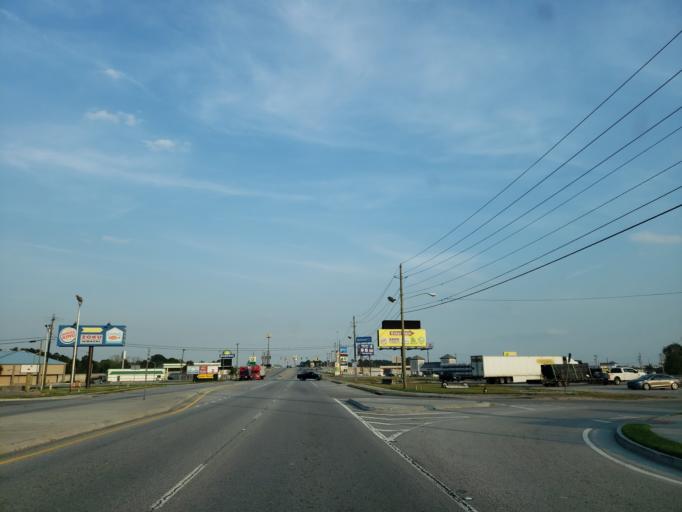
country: US
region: Georgia
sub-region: Cook County
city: Adel
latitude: 31.1380
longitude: -83.4430
